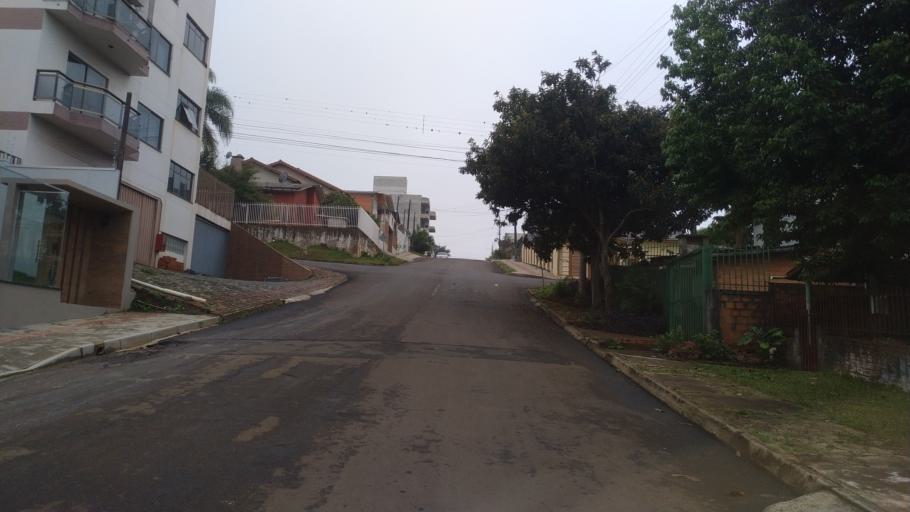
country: BR
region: Santa Catarina
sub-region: Chapeco
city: Chapeco
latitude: -27.0797
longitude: -52.6289
